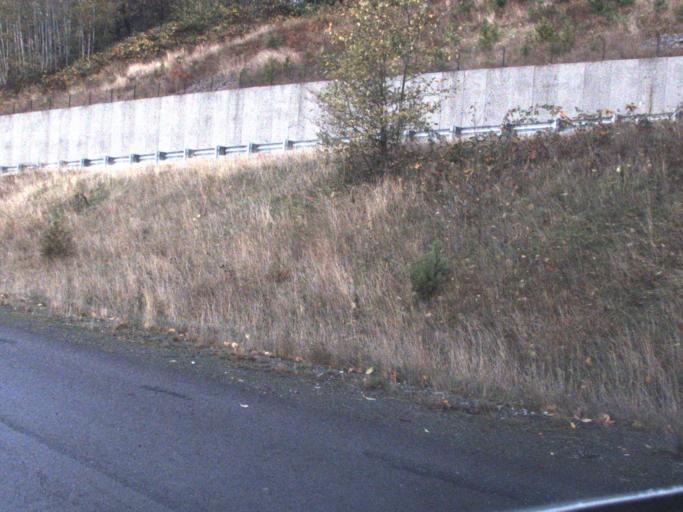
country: US
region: Washington
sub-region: Snohomish County
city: Fobes Hill
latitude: 47.9620
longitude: -122.1236
